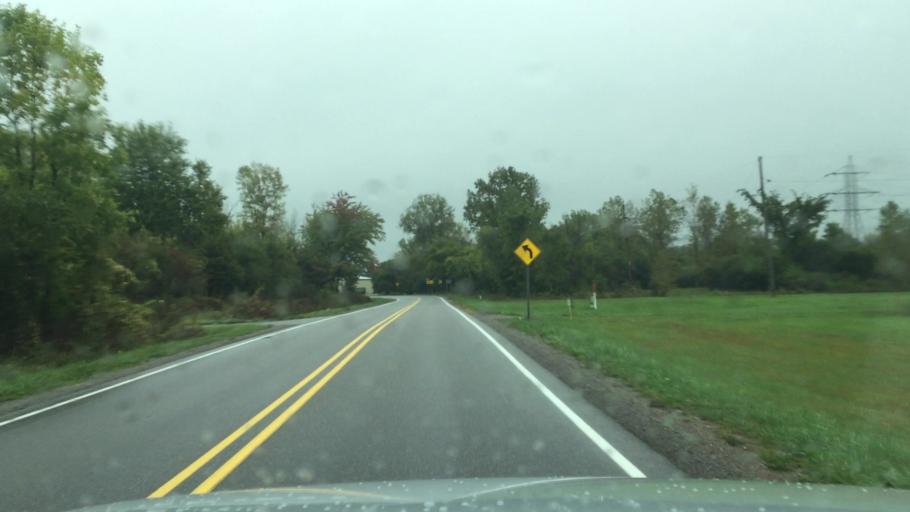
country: US
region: Michigan
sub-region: Saginaw County
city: Buena Vista
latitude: 43.3932
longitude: -83.9184
